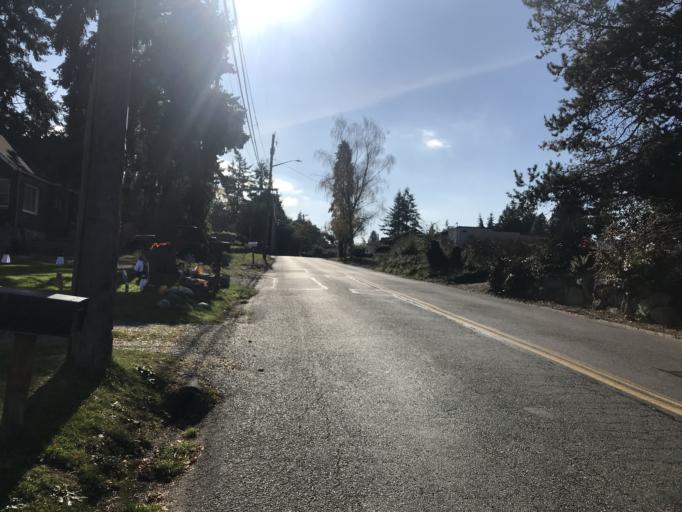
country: US
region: Washington
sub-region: Pierce County
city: University Place
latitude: 47.2460
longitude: -122.5525
